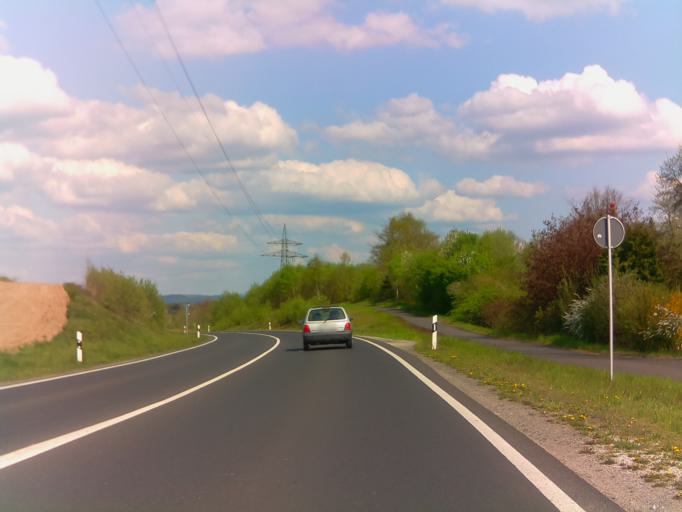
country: DE
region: Bavaria
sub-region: Upper Franconia
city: Neustadt bei Coburg
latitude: 50.3131
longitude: 11.1294
